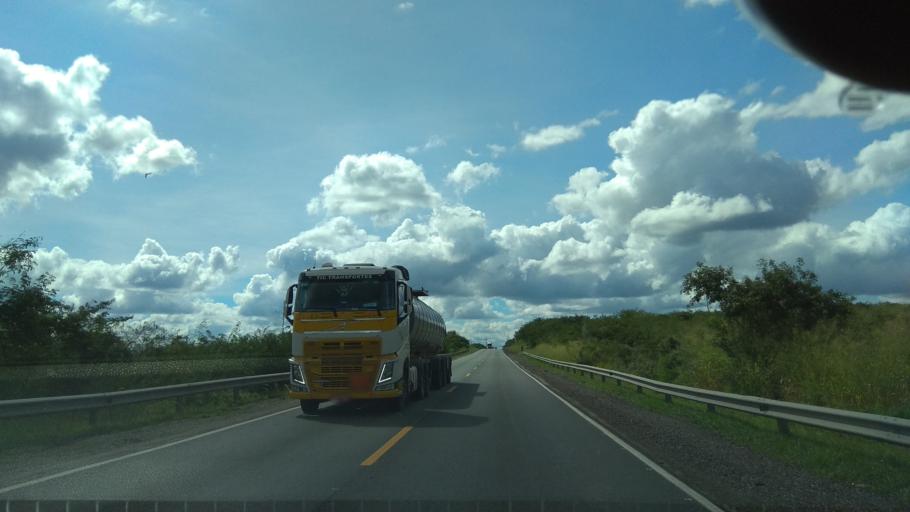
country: BR
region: Bahia
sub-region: Jaguaquara
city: Jaguaquara
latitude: -13.4387
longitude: -40.0297
